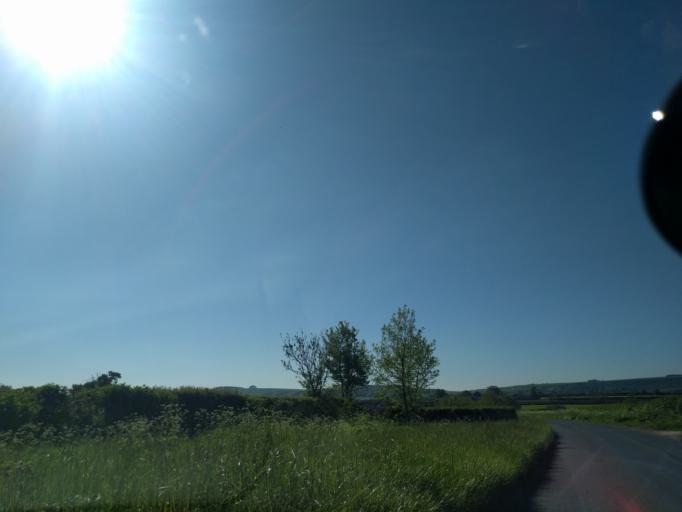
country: GB
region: England
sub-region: Wiltshire
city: Bratton
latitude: 51.2977
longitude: -2.1349
